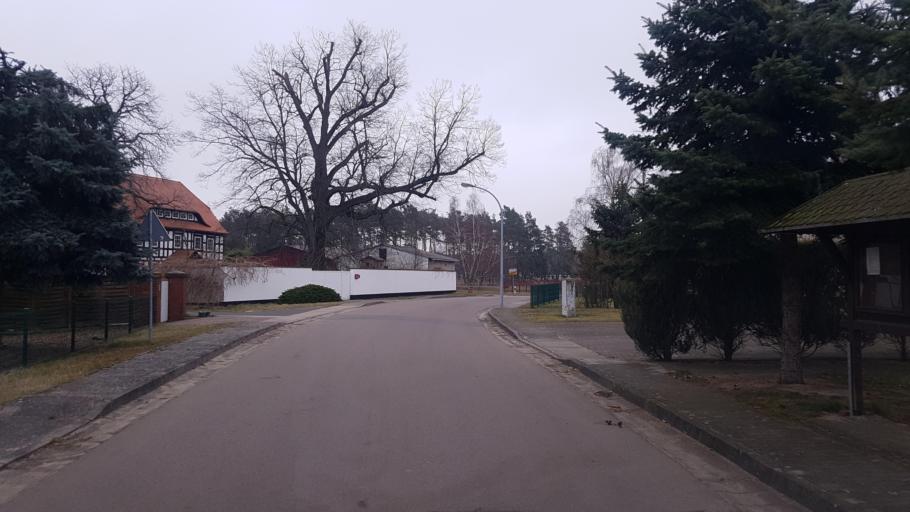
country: DE
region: Brandenburg
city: Herzberg
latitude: 51.6962
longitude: 13.1769
